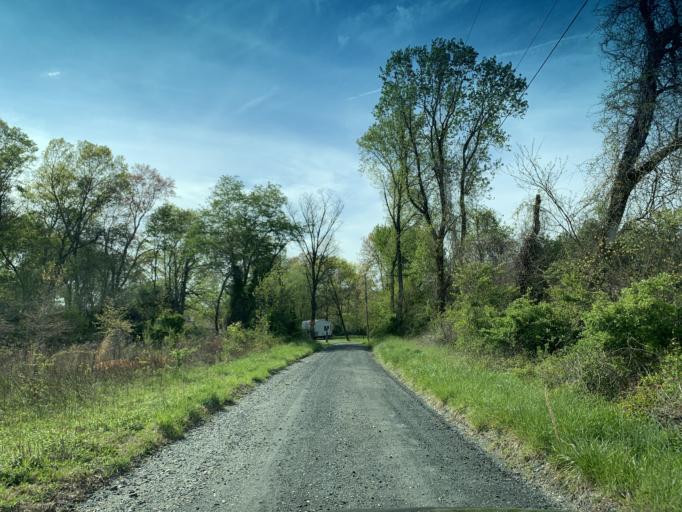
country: US
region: Maryland
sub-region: Harford County
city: Perryman
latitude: 39.4719
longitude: -76.2176
